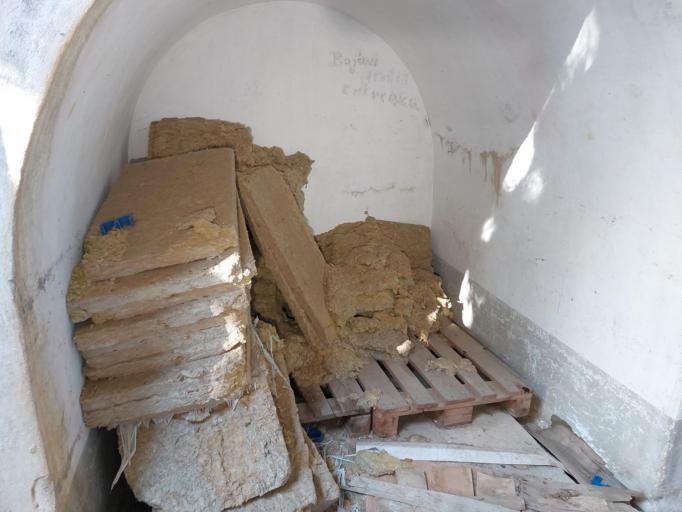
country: HR
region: Dubrovacko-Neretvanska
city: Smokvica
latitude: 42.7247
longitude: 16.8437
